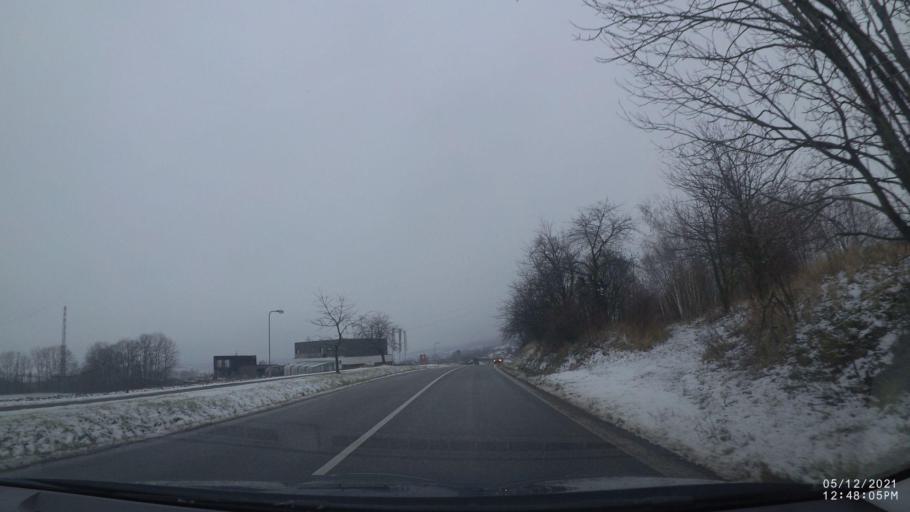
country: CZ
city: Nove Mesto nad Metuji
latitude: 50.3637
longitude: 16.1457
